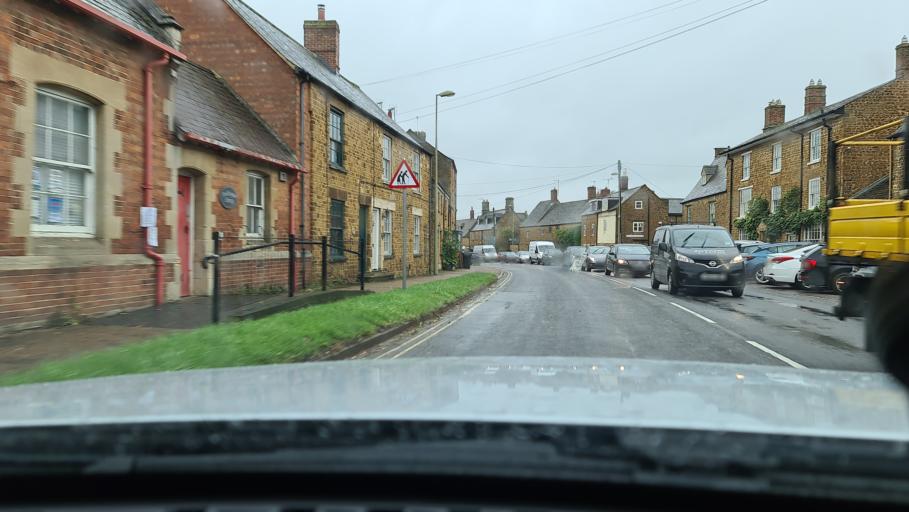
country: GB
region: England
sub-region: Oxfordshire
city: Deddington
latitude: 51.9821
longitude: -1.3233
